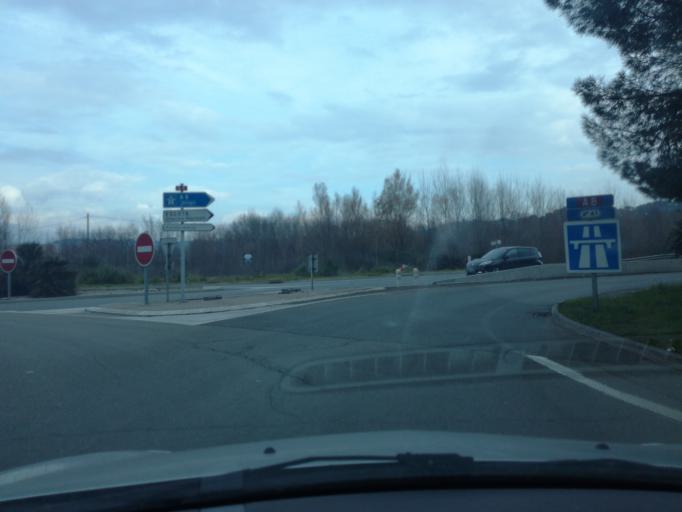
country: FR
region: Provence-Alpes-Cote d'Azur
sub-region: Departement des Alpes-Maritimes
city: Mandelieu-la-Napoule
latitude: 43.5608
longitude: 6.9511
